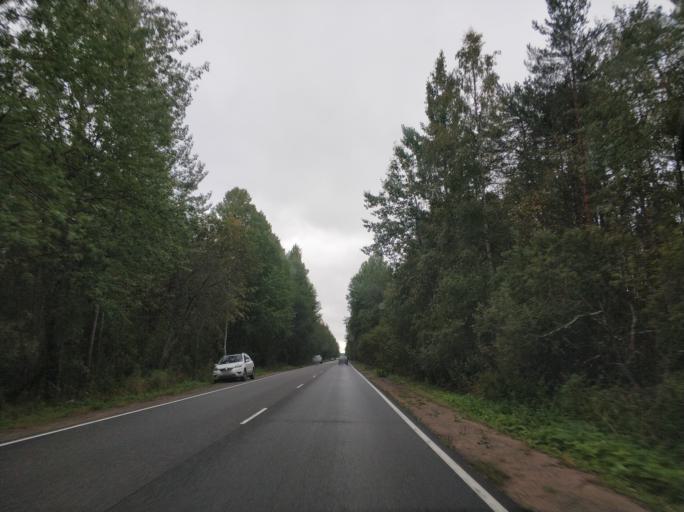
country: RU
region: Leningrad
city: Borisova Griva
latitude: 60.1508
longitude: 30.9370
